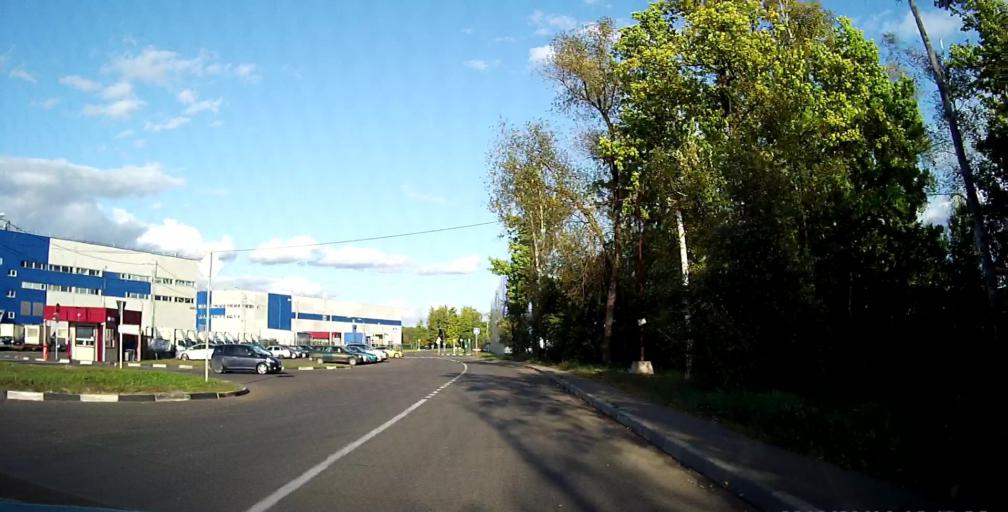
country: RU
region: Moskovskaya
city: Klimovsk
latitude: 55.3616
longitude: 37.5603
